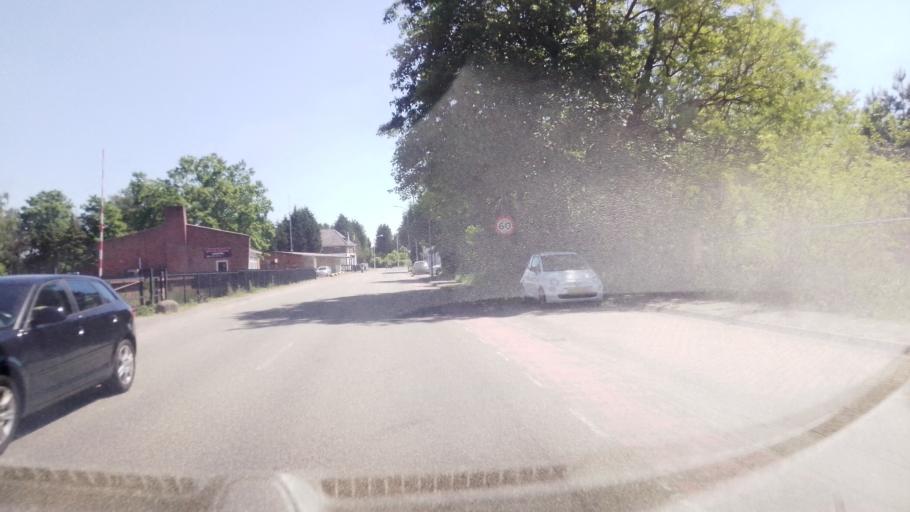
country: NL
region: Limburg
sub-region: Gemeente Venlo
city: Tegelen
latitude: 51.3307
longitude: 6.1673
